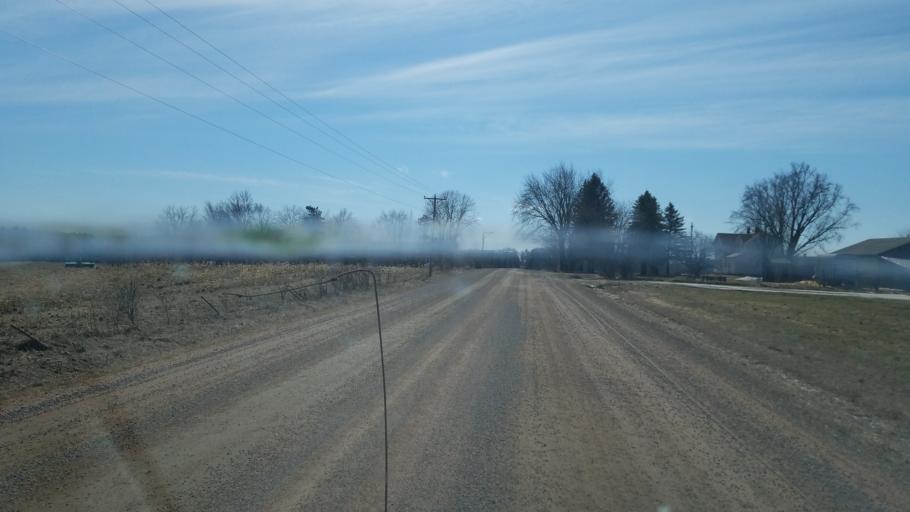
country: US
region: Wisconsin
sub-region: Clark County
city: Loyal
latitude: 44.6019
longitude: -90.4565
